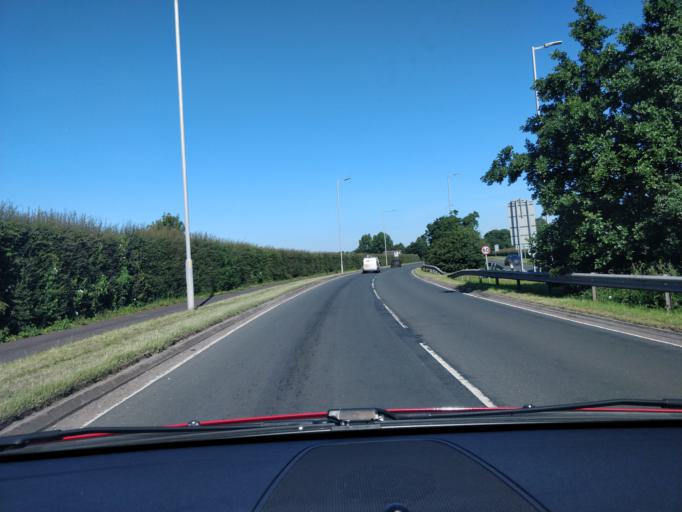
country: GB
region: England
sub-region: Lancashire
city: Banks
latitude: 53.6633
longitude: -2.8912
